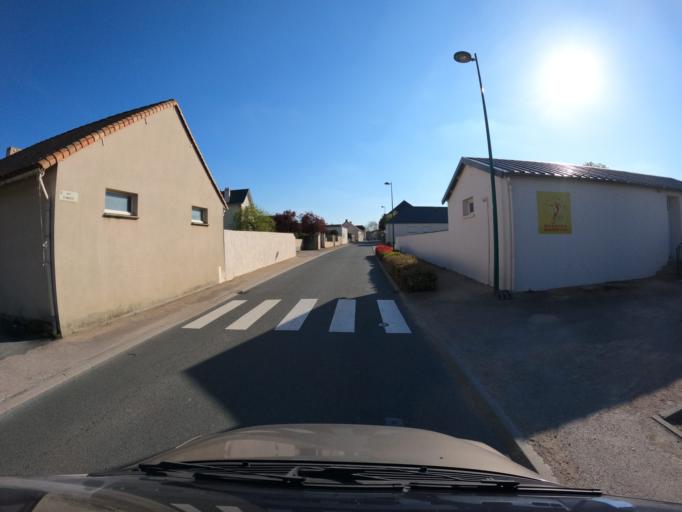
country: FR
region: Pays de la Loire
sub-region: Departement de la Vendee
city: Beaurepaire
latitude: 46.9089
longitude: -1.1310
